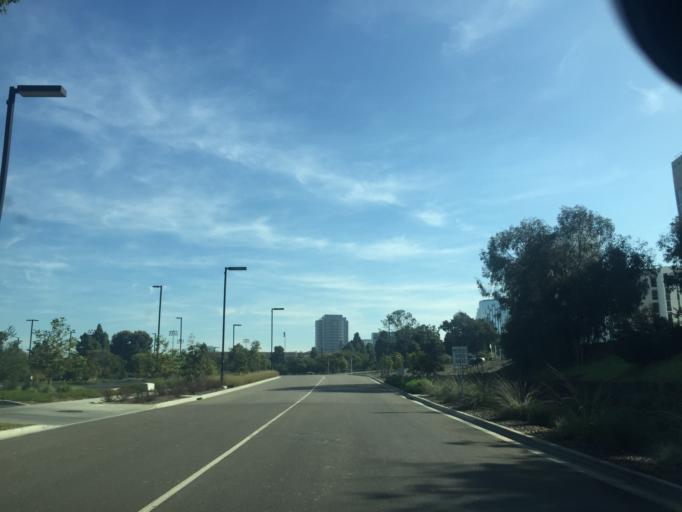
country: US
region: California
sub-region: San Diego County
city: La Jolla
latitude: 32.8759
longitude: -117.2208
